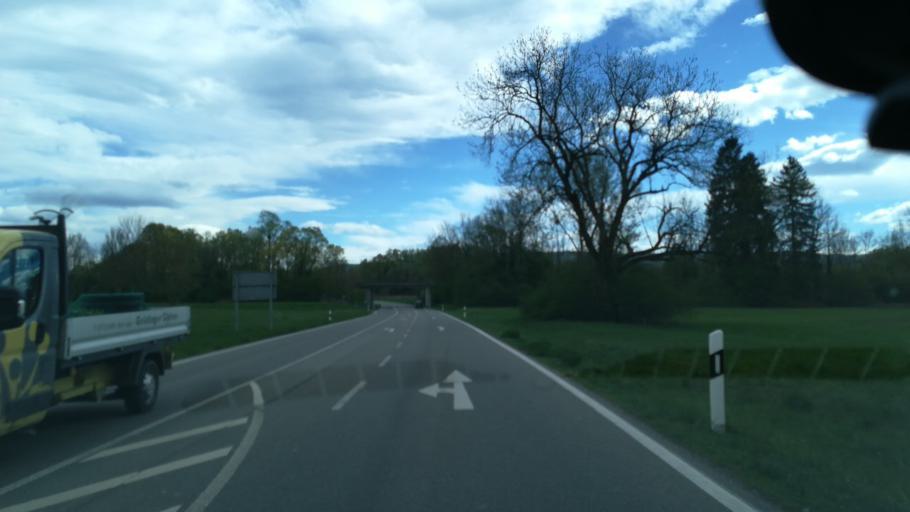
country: DE
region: Baden-Wuerttemberg
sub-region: Freiburg Region
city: Moos
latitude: 47.7513
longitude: 8.9227
